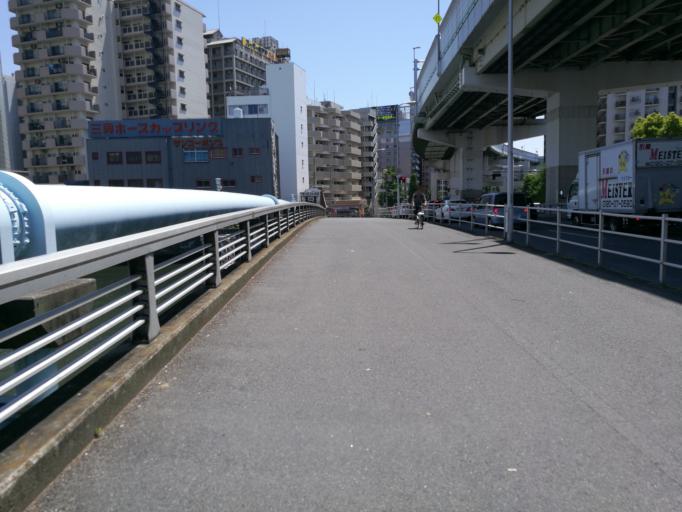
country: JP
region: Osaka
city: Osaka-shi
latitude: 34.6861
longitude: 135.4837
